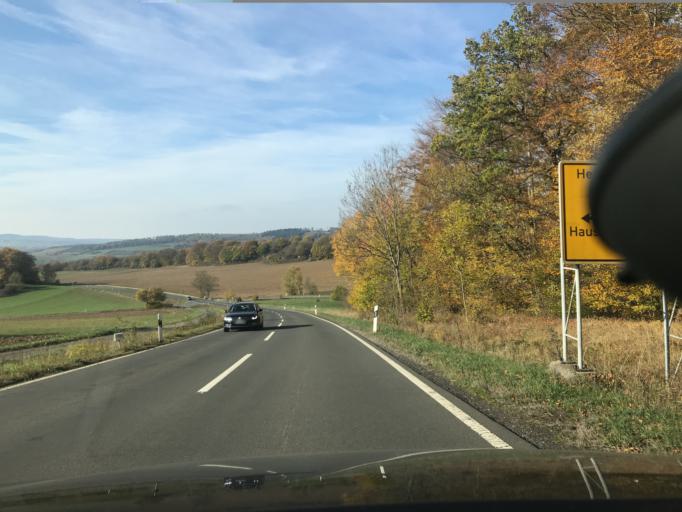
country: DE
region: Hesse
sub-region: Regierungsbezirk Kassel
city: Grossalmerode
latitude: 51.2144
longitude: 9.8239
